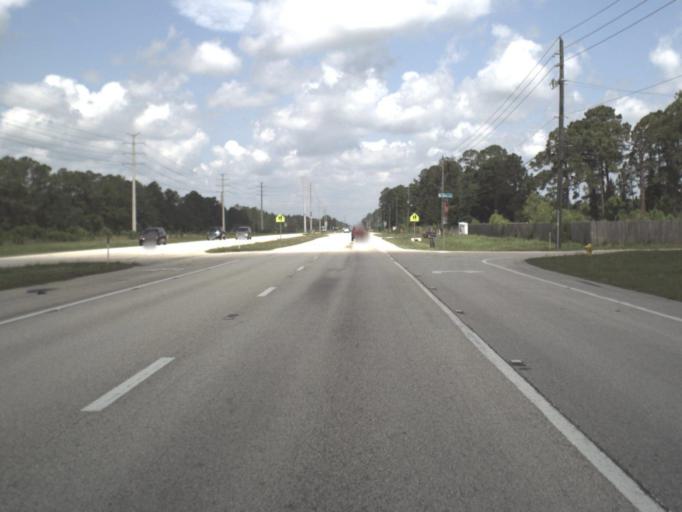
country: US
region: Florida
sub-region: Saint Johns County
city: Palm Valley
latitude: 30.0714
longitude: -81.4450
